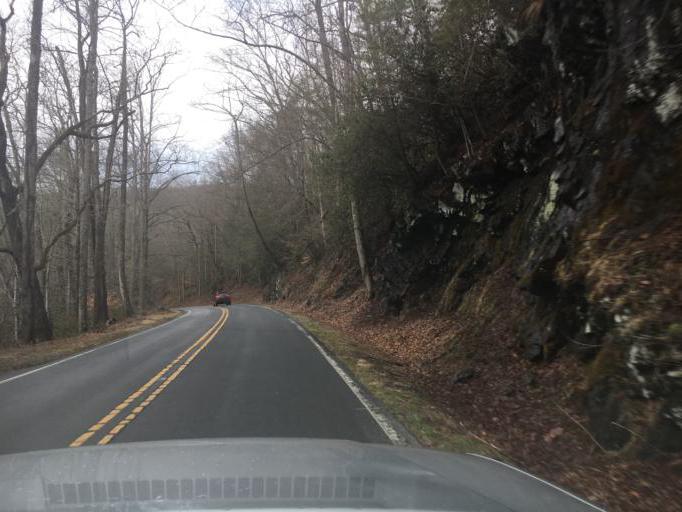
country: US
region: North Carolina
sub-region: Transylvania County
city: Brevard
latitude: 35.2870
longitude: -82.7329
